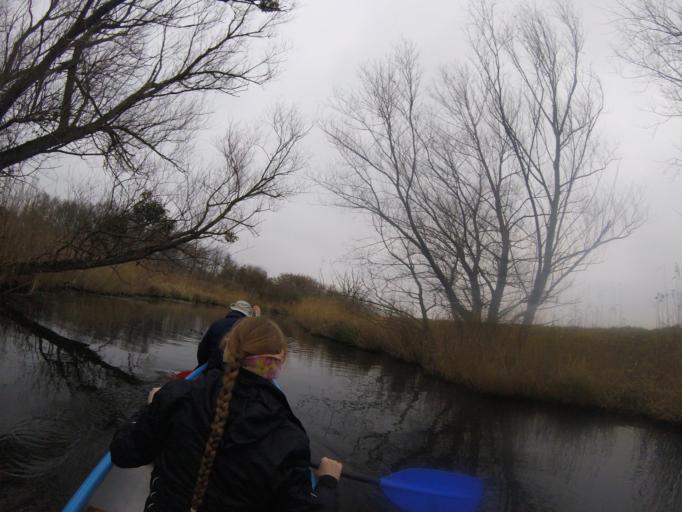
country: HU
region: Zala
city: Keszthely
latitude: 46.7583
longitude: 17.2101
